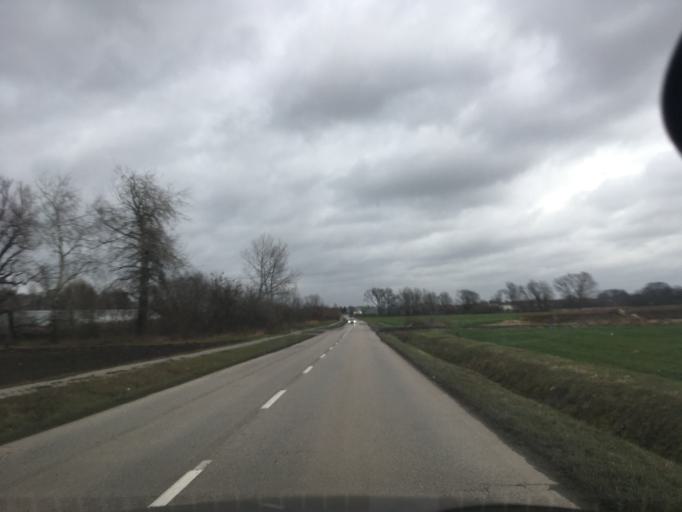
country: PL
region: Masovian Voivodeship
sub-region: Powiat pruszkowski
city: Rybie
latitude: 52.1302
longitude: 20.9670
